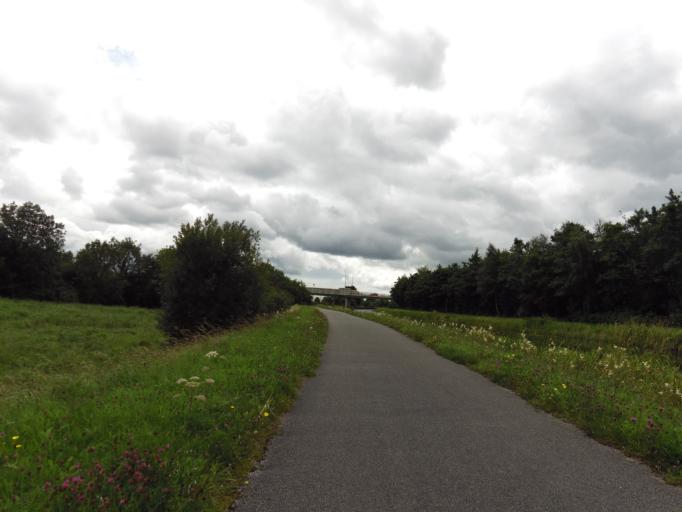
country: IE
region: Leinster
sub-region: An Iarmhi
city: An Muileann gCearr
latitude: 53.5187
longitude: -7.3666
